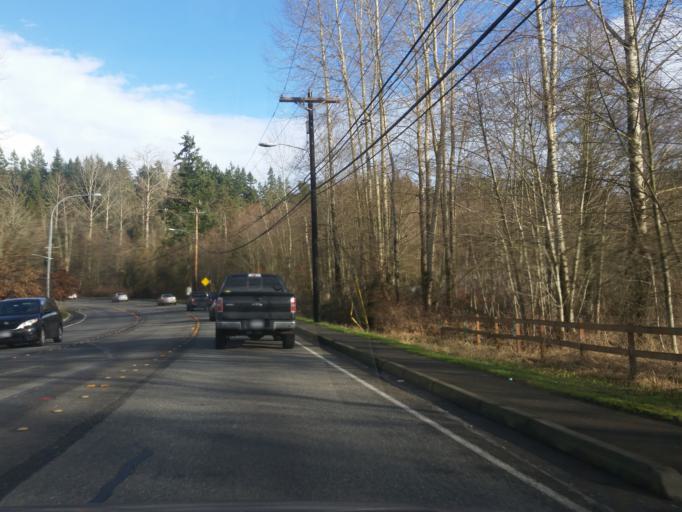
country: US
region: Washington
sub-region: Snohomish County
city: North Creek
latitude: 47.8094
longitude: -122.2038
